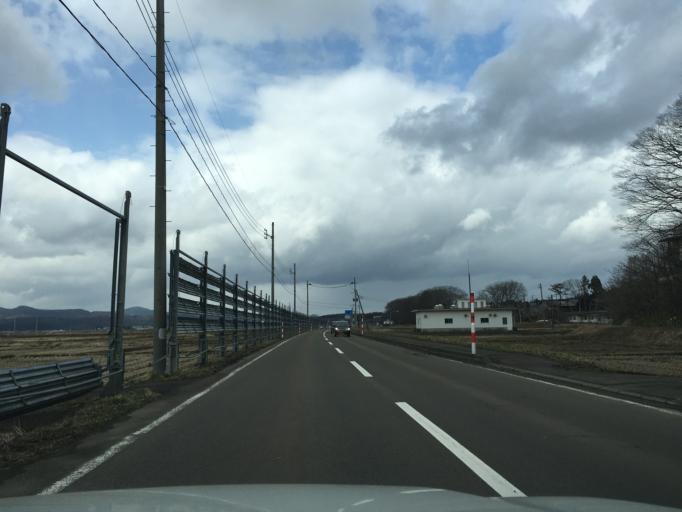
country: JP
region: Akita
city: Takanosu
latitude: 40.1475
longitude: 140.3422
